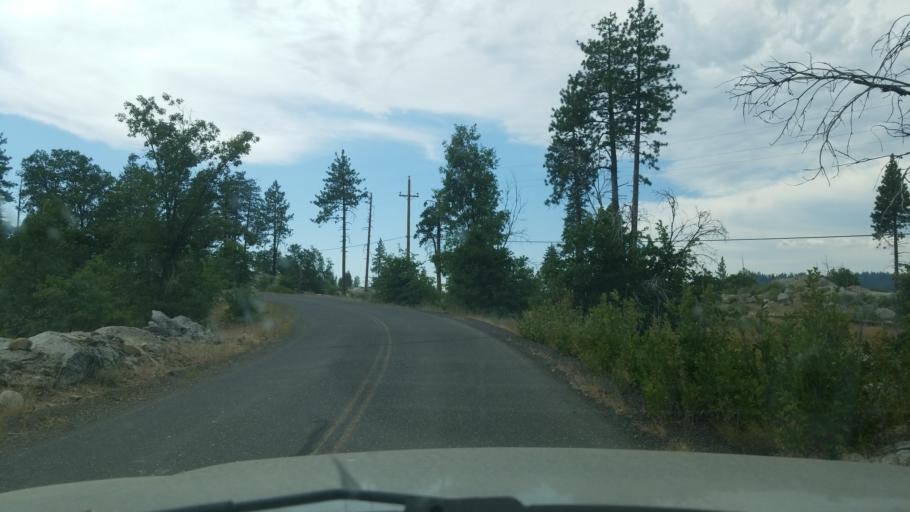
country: US
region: California
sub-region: Mariposa County
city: Yosemite Valley
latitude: 37.9026
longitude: -119.8123
